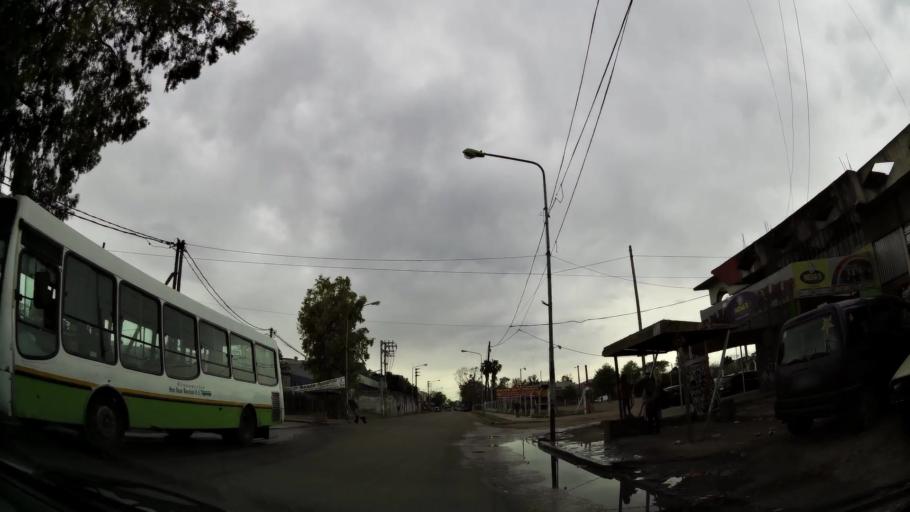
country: AR
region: Buenos Aires
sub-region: Partido de Quilmes
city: Quilmes
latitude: -34.7888
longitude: -58.2599
